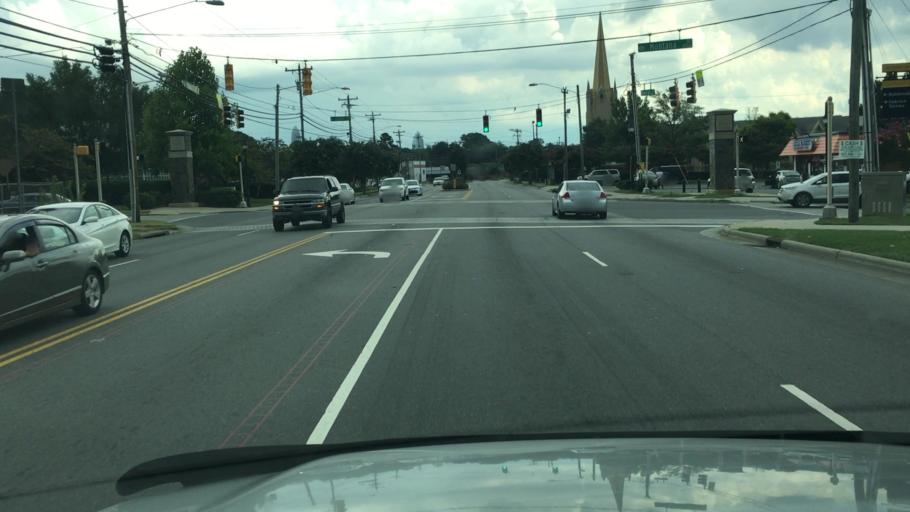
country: US
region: North Carolina
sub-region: Mecklenburg County
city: Charlotte
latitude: 35.2687
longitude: -80.8540
